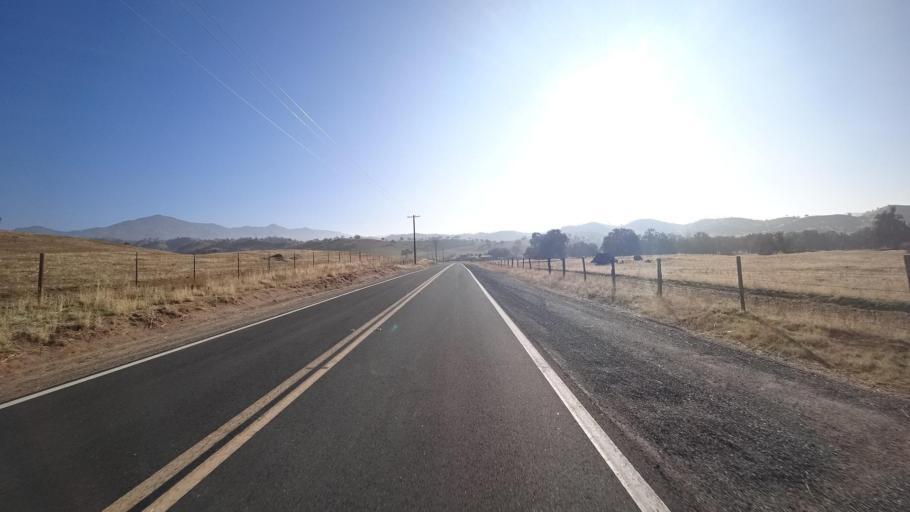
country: US
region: California
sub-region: Tulare County
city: Richgrove
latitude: 35.7380
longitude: -118.8623
